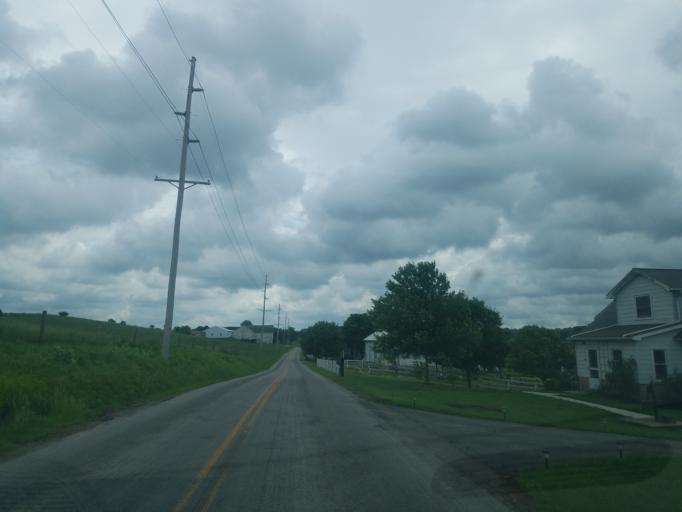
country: US
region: Ohio
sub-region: Tuscarawas County
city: Sugarcreek
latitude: 40.5318
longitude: -81.7338
